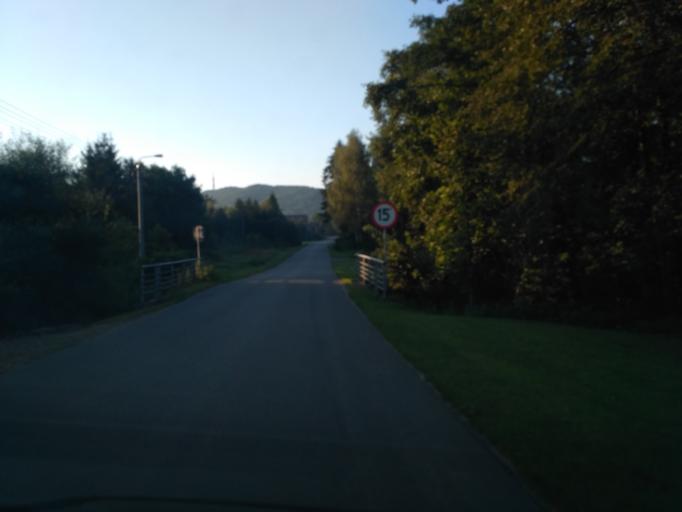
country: PL
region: Subcarpathian Voivodeship
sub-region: Powiat krosnienski
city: Odrzykon
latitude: 49.7751
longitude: 21.7794
